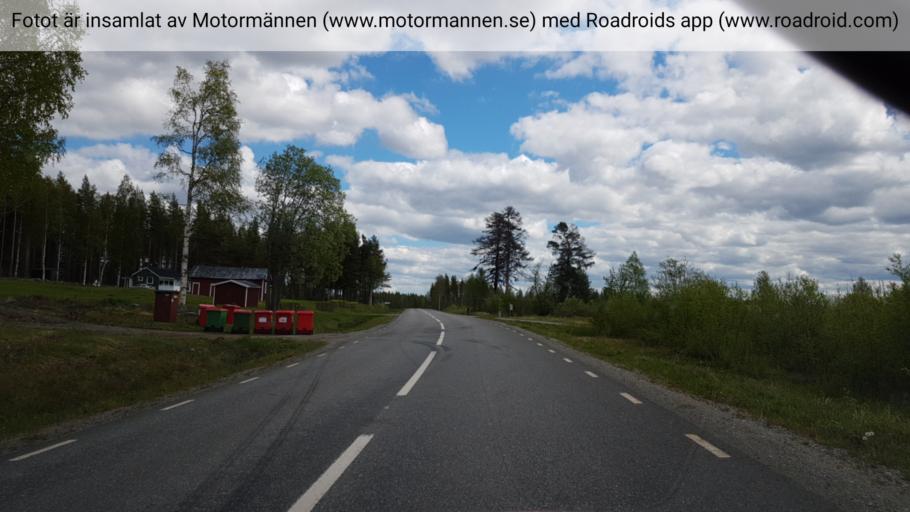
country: SE
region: Vaesterbotten
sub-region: Norsjo Kommun
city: Norsjoe
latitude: 64.8344
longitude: 19.7809
